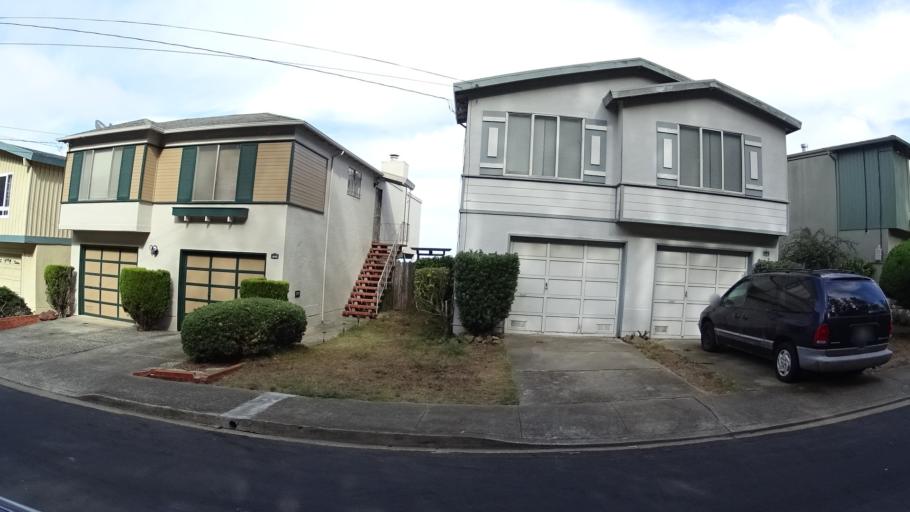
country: US
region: California
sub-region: San Mateo County
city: Daly City
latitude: 37.7034
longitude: -122.4285
